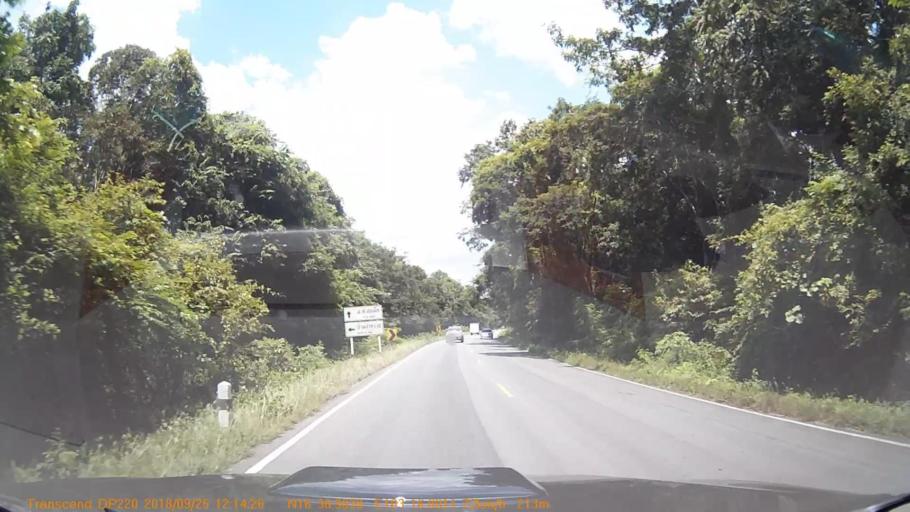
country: TH
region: Kalasin
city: Huai Mek
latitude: 16.5151
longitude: 103.2667
